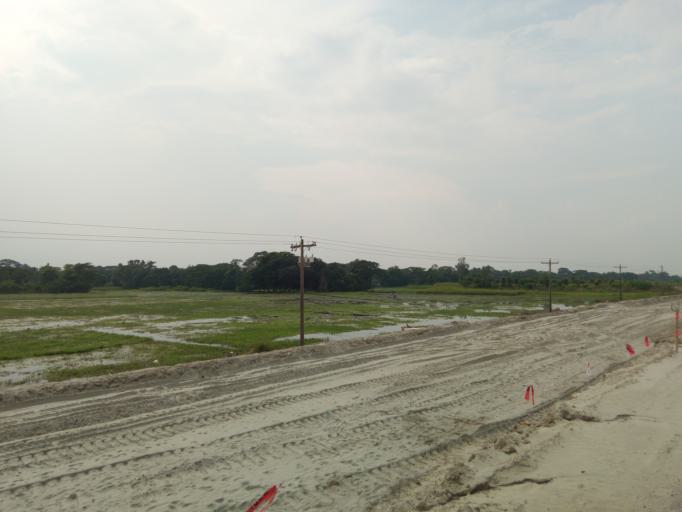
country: BD
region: Dhaka
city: Dohar
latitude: 23.5589
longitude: 90.2990
